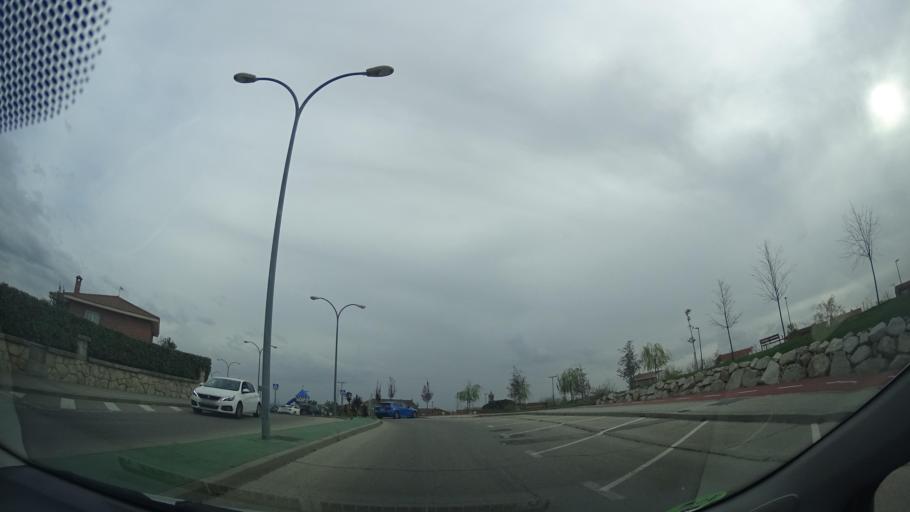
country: ES
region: Madrid
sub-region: Provincia de Madrid
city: Colmenar Viejo
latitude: 40.6646
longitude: -3.7649
